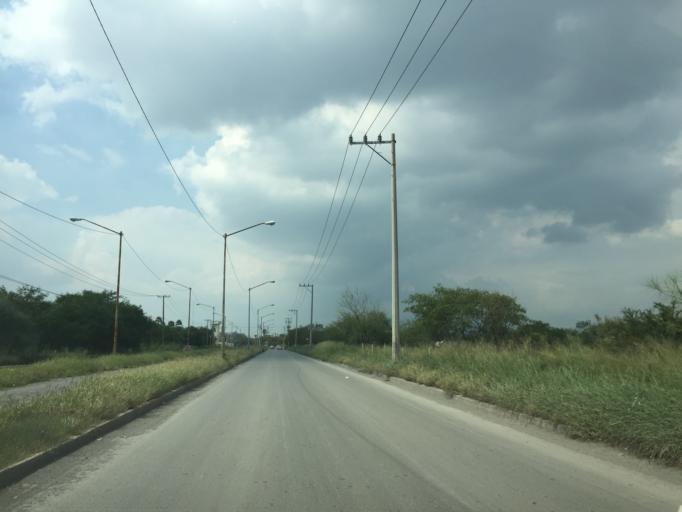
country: MX
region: Nuevo Leon
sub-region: Apodaca
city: Fraccionamiento Cosmopolis Octavo Sector
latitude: 25.8102
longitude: -100.2687
